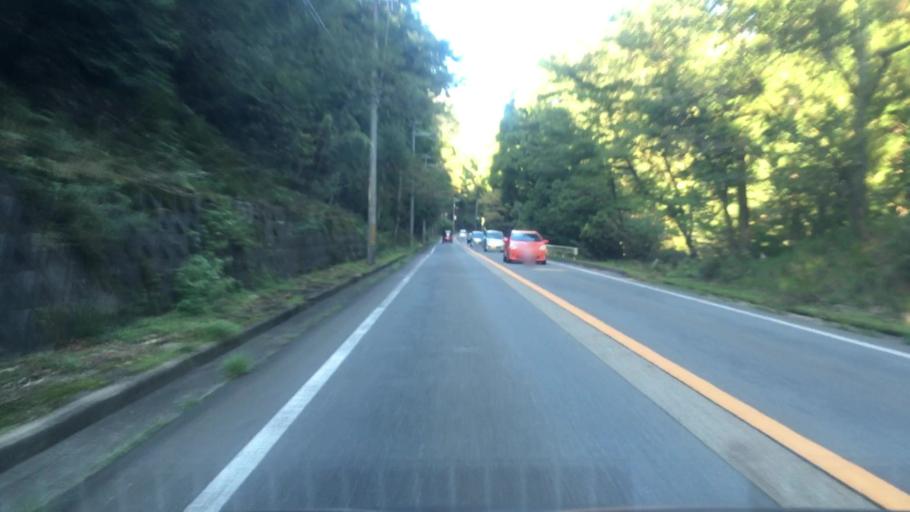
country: JP
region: Hyogo
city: Toyooka
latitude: 35.5786
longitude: 134.8559
